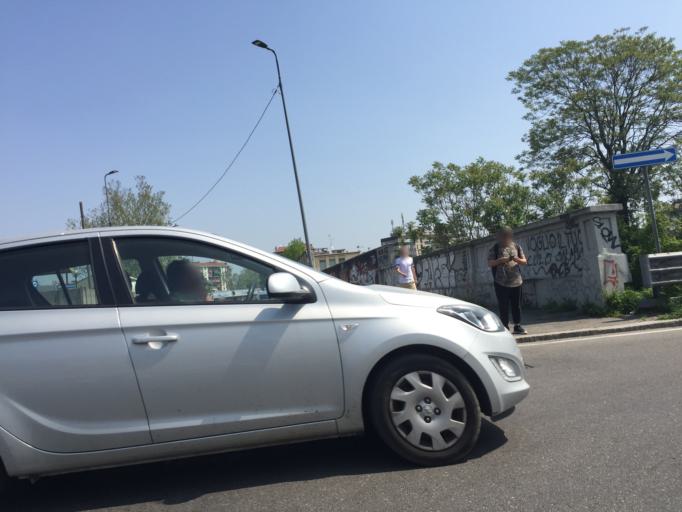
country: IT
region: Lombardy
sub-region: Citta metropolitana di Milano
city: Milano
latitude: 45.4428
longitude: 9.1598
